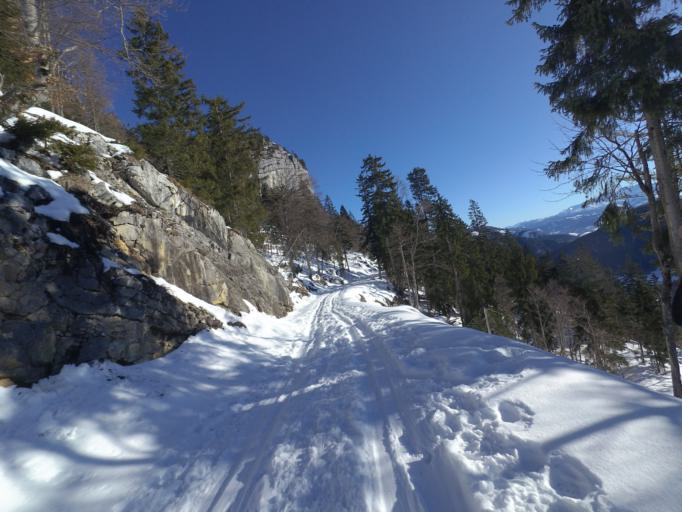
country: AT
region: Salzburg
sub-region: Politischer Bezirk Hallein
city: Scheffau am Tennengebirge
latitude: 47.6333
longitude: 13.2559
